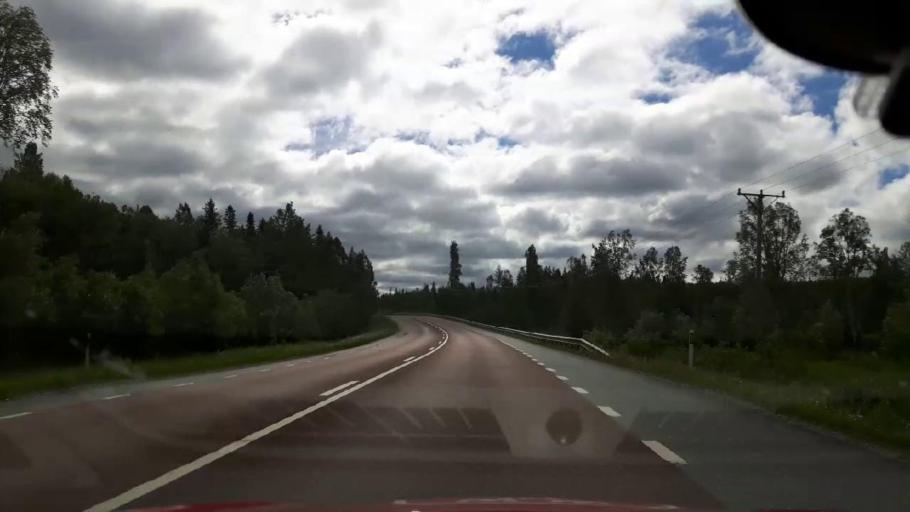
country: SE
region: Jaemtland
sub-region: Braecke Kommun
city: Braecke
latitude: 62.9478
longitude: 15.1658
